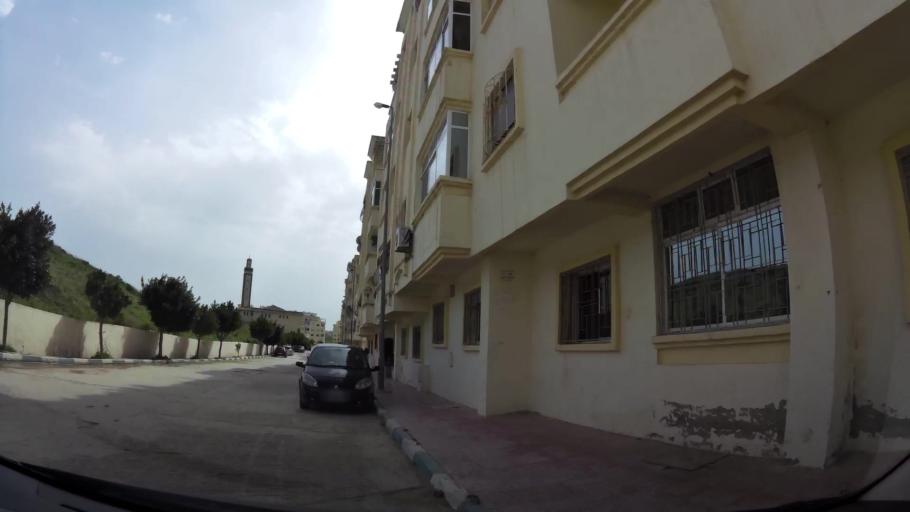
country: MA
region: Tanger-Tetouan
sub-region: Tanger-Assilah
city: Boukhalef
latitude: 35.7408
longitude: -5.8667
